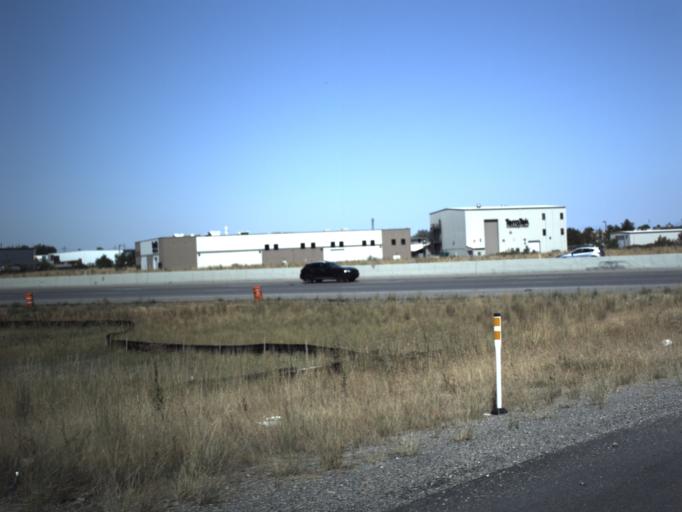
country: US
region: Utah
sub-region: Salt Lake County
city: West Valley City
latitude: 40.7250
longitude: -111.9536
